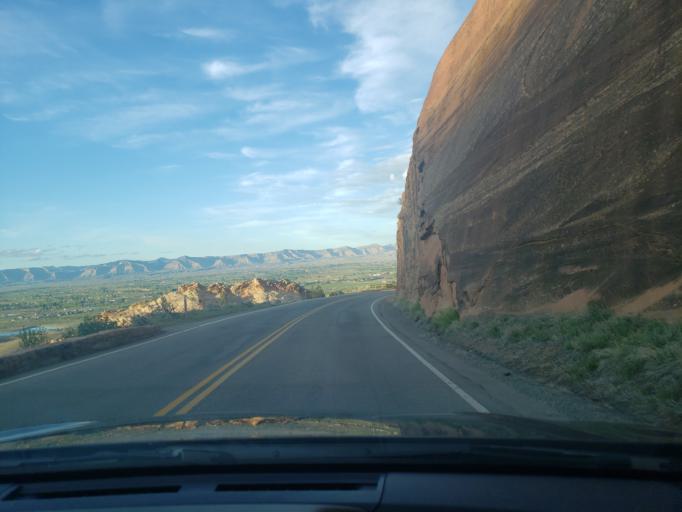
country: US
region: Colorado
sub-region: Mesa County
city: Fruita
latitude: 39.1156
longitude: -108.7293
